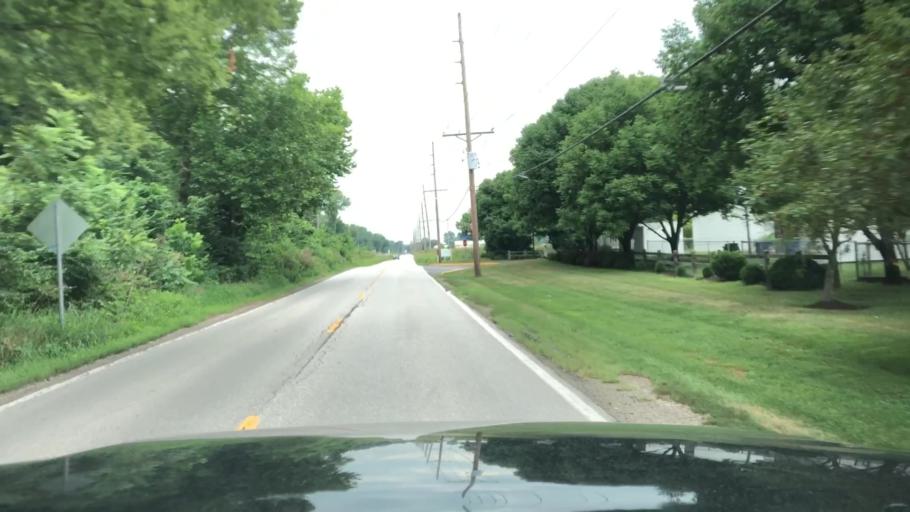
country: US
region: Missouri
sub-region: Saint Charles County
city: Saint Charles
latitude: 38.8152
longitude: -90.5237
